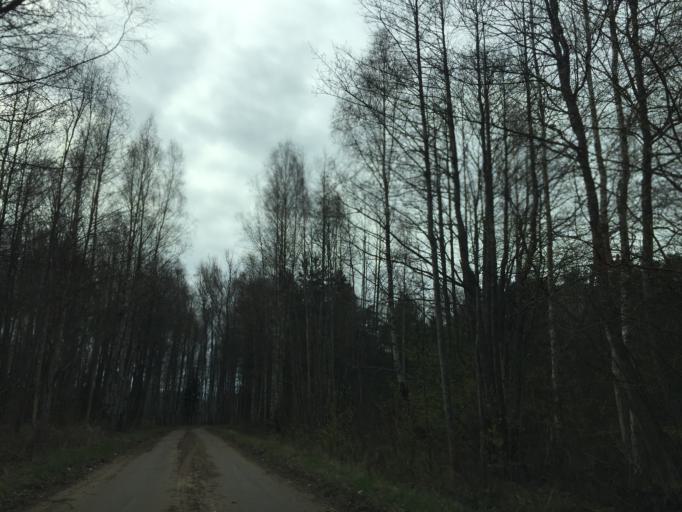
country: LV
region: Salacgrivas
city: Salacgriva
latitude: 57.5417
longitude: 24.3673
